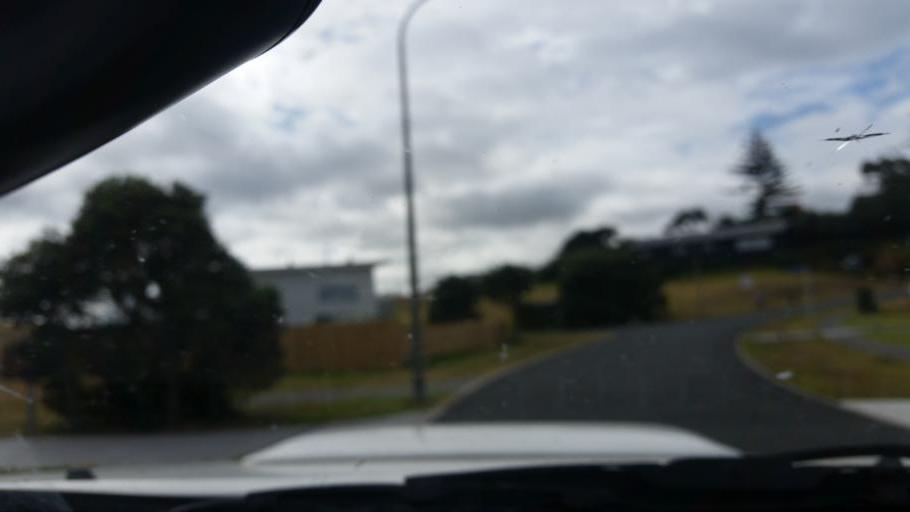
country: NZ
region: Northland
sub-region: Kaipara District
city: Dargaville
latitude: -35.9486
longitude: 173.7482
